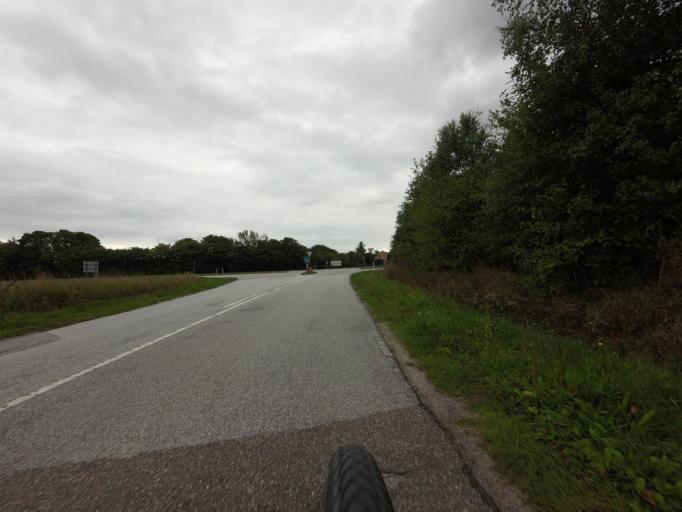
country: DK
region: North Denmark
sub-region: Hjorring Kommune
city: Hirtshals
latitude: 57.5652
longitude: 10.0323
